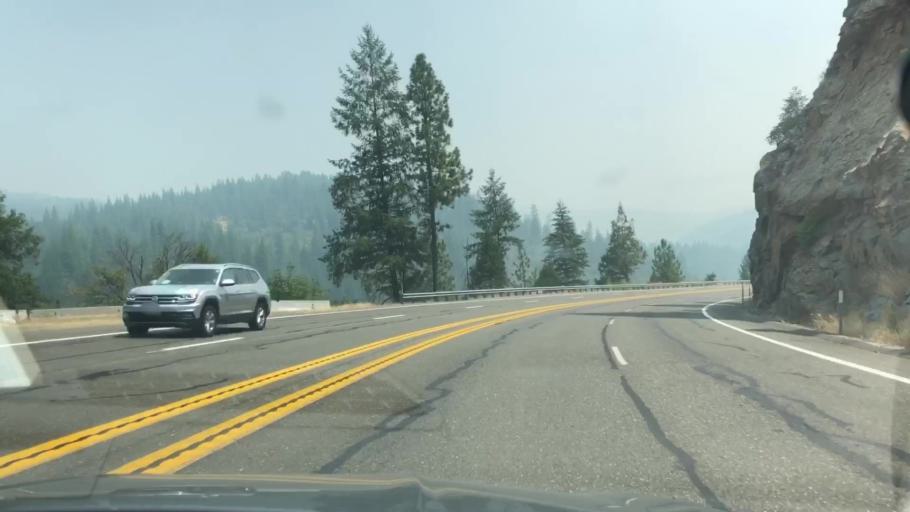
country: US
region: California
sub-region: El Dorado County
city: Pollock Pines
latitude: 38.7666
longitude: -120.4968
